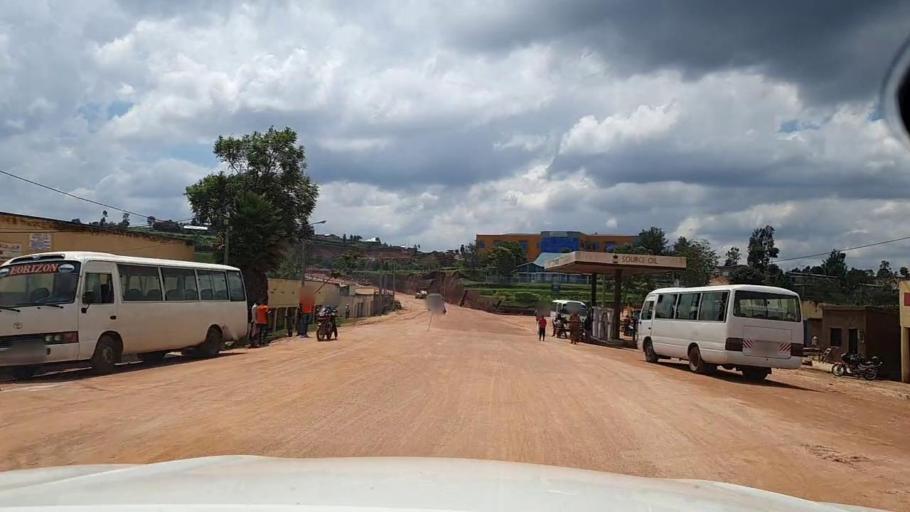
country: RW
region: Southern Province
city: Butare
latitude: -2.6968
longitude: 29.5700
